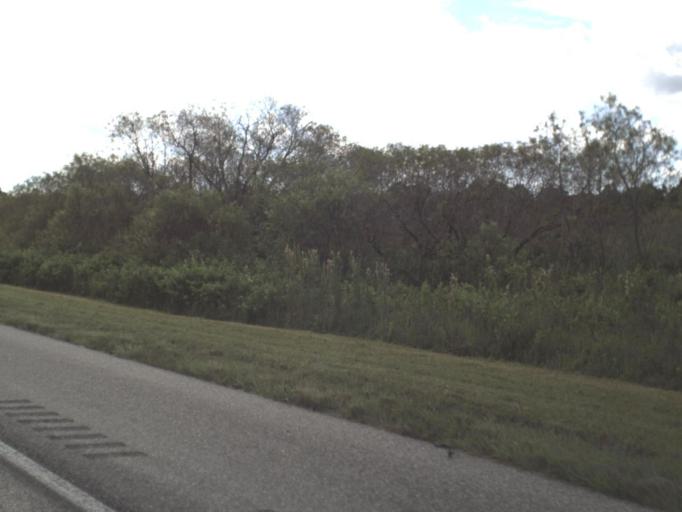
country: US
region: Florida
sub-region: Sarasota County
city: North Port
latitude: 27.0984
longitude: -82.1435
